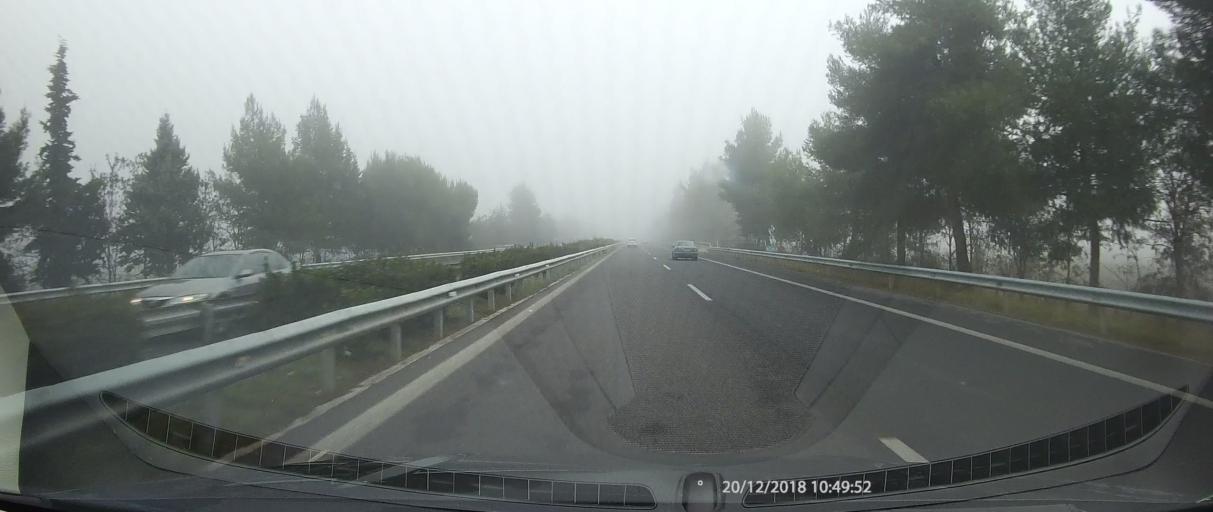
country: GR
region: Peloponnese
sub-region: Nomos Arkadias
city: Tripoli
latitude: 37.5501
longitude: 22.4194
